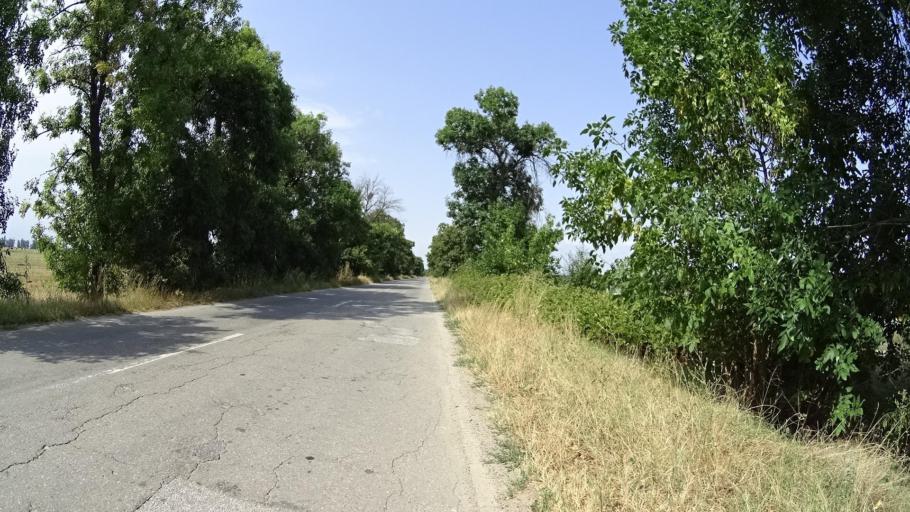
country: BG
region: Plovdiv
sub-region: Obshtina Kaloyanovo
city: Kaloyanovo
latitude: 42.2582
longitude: 24.7997
